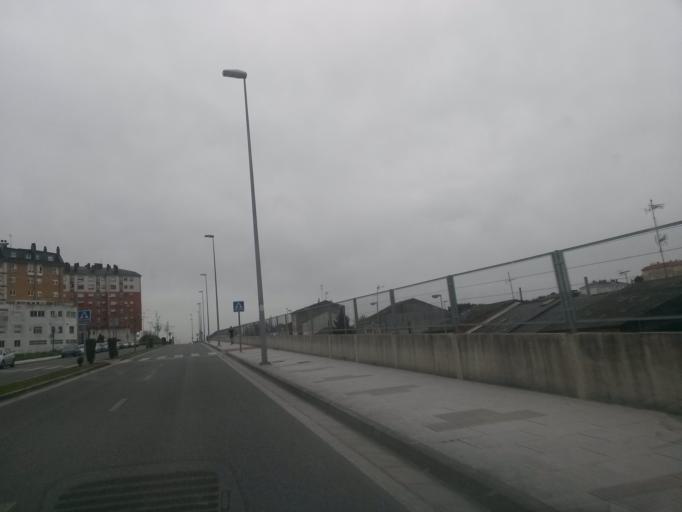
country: ES
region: Galicia
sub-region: Provincia de Lugo
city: Lugo
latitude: 43.0209
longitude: -7.5576
